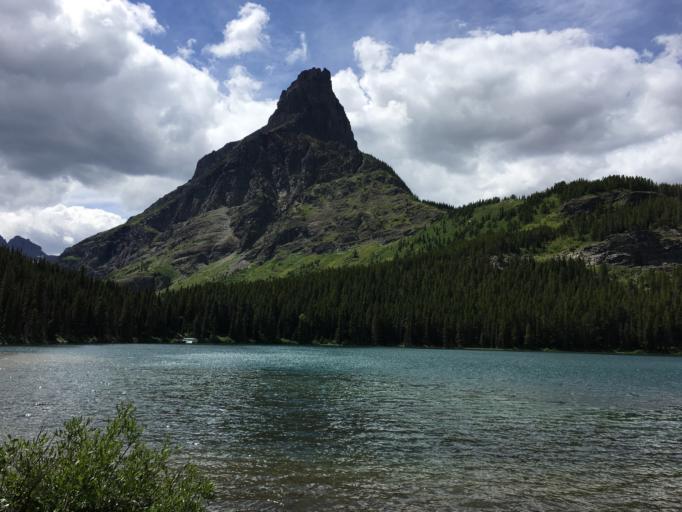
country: CA
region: Alberta
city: Cardston
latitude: 48.7901
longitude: -113.6622
